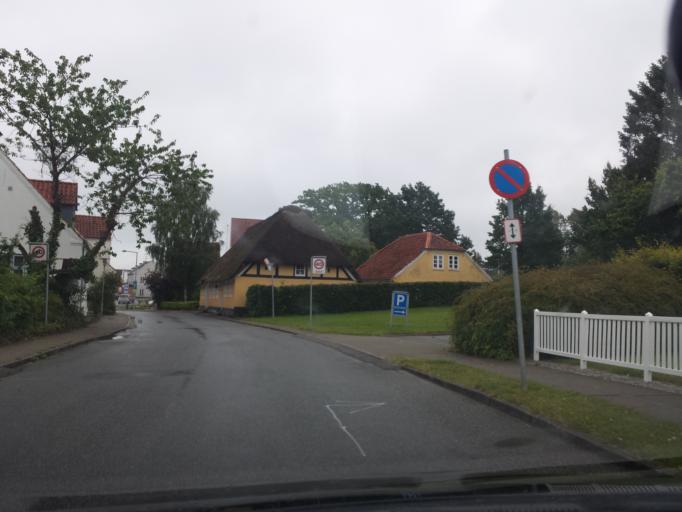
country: DK
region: South Denmark
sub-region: Sonderborg Kommune
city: Grasten
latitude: 54.9205
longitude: 9.5892
